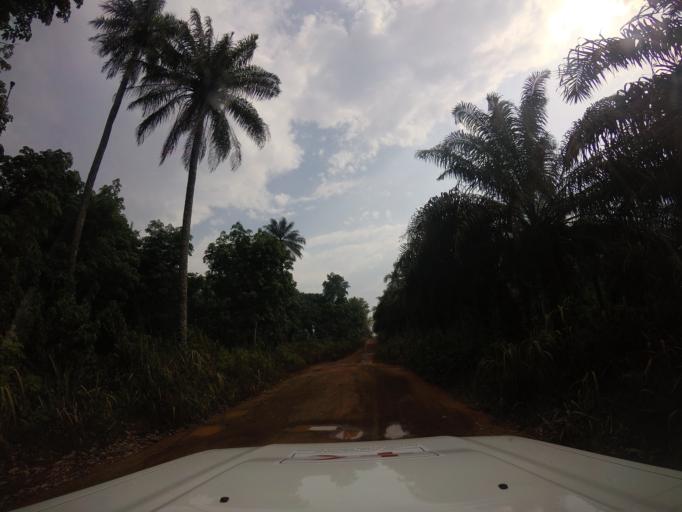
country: SL
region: Southern Province
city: Zimmi
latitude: 7.0284
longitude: -11.2880
